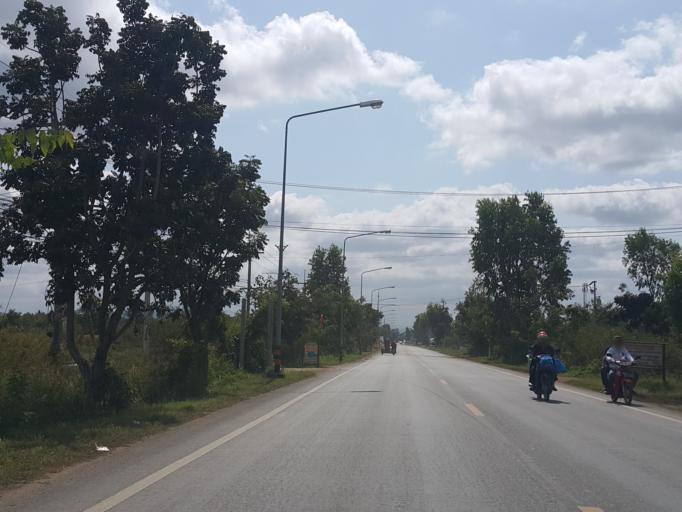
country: TH
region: Lamphun
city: Ban Thi
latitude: 18.5879
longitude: 99.0804
